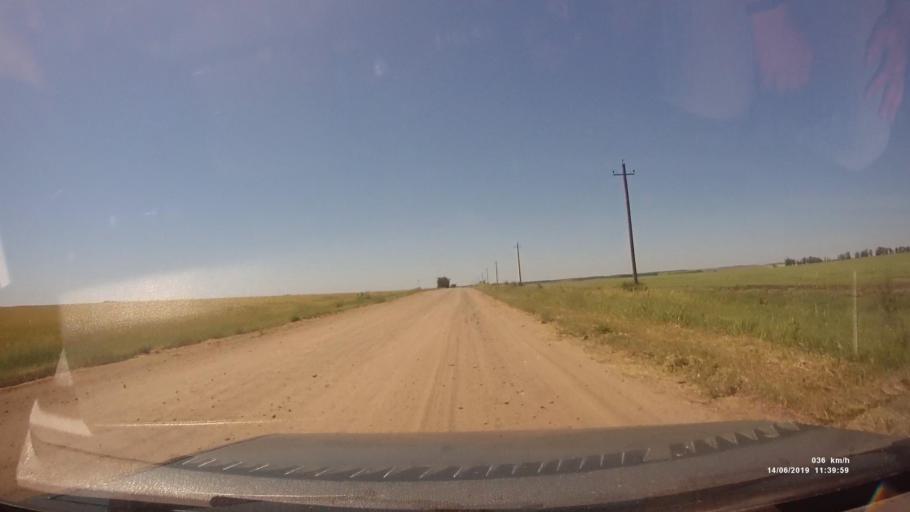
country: RU
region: Rostov
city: Kazanskaya
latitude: 49.8686
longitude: 41.3631
